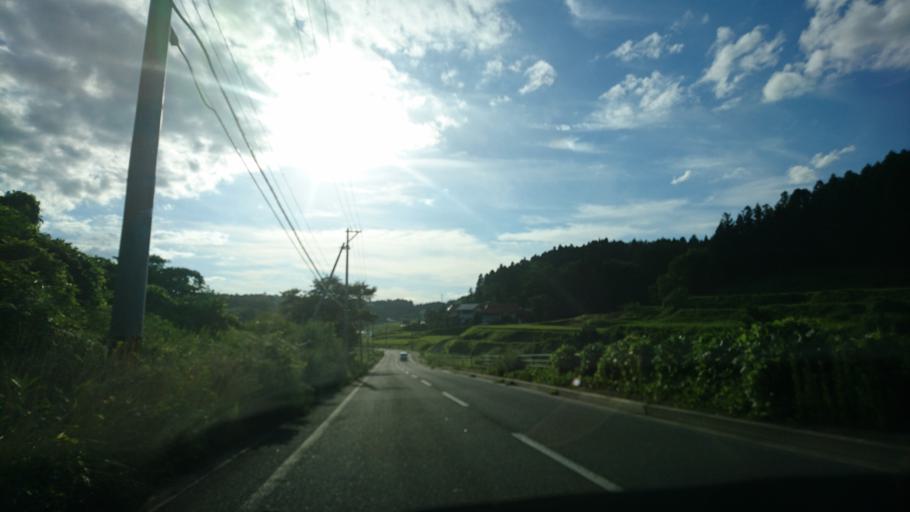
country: JP
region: Iwate
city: Ichinoseki
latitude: 38.8668
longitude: 141.1927
